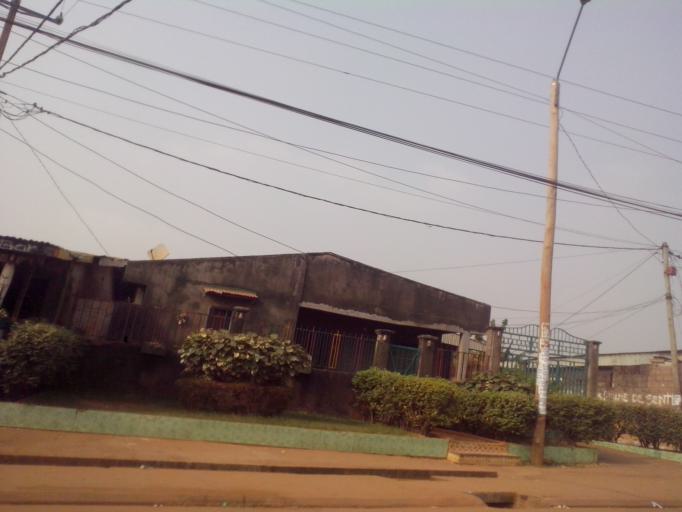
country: CM
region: Centre
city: Yaounde
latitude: 3.8462
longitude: 11.4975
